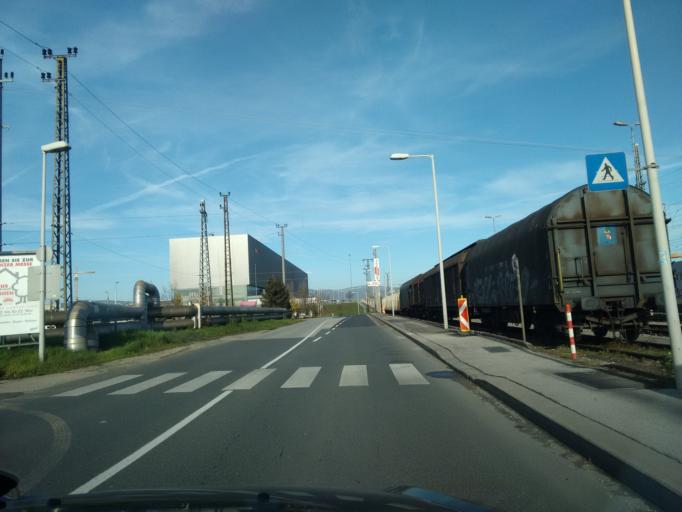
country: AT
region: Upper Austria
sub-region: Linz Stadt
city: Linz
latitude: 48.2758
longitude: 14.3170
